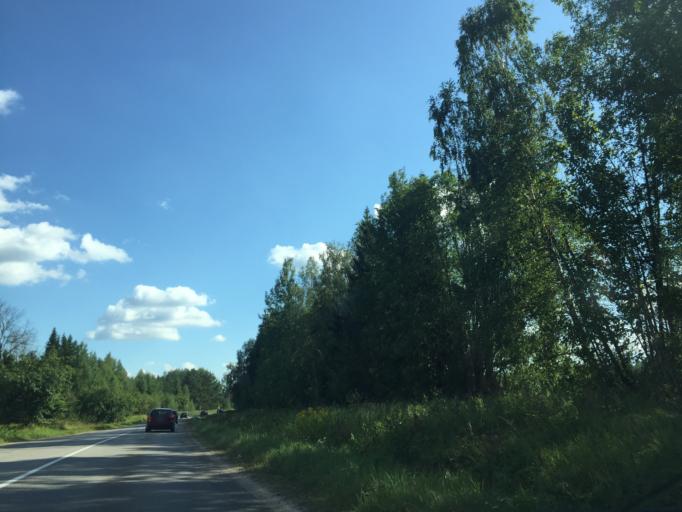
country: LV
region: Beverina
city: Murmuiza
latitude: 57.4390
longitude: 25.4410
